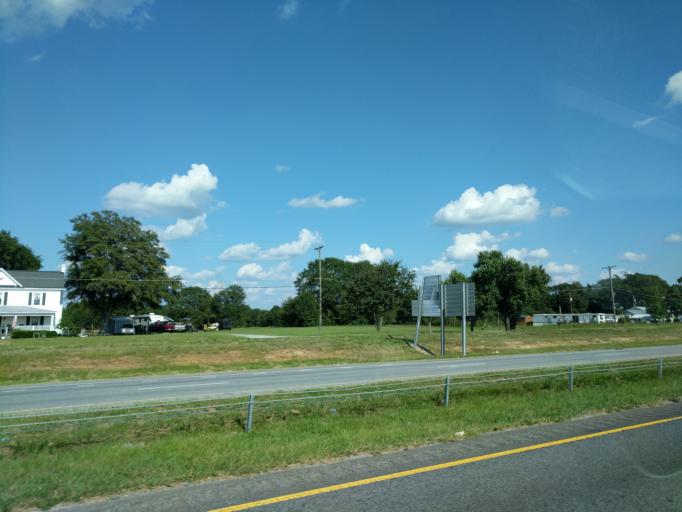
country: US
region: South Carolina
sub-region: Greenville County
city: Fountain Inn
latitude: 34.6630
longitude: -82.1747
